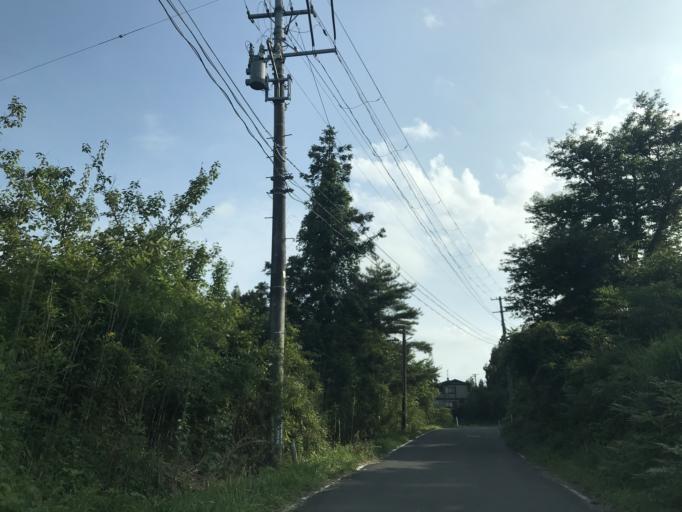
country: JP
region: Iwate
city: Ichinoseki
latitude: 38.8626
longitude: 141.1221
